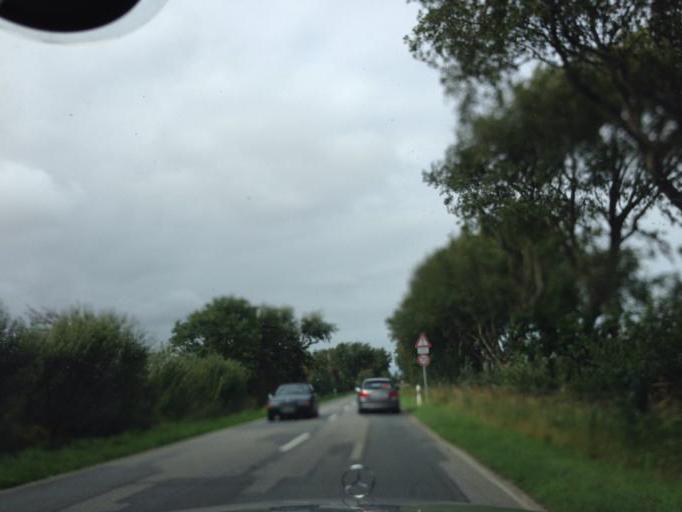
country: DE
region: Schleswig-Holstein
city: Galmsbull
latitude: 54.7694
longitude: 8.7512
